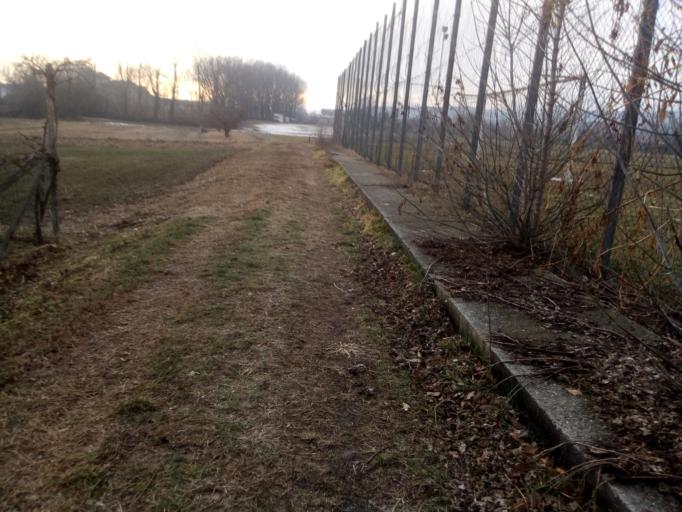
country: IT
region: Piedmont
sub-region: Provincia di Torino
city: Cascinette d'Ivrea
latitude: 45.4745
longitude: 7.9019
